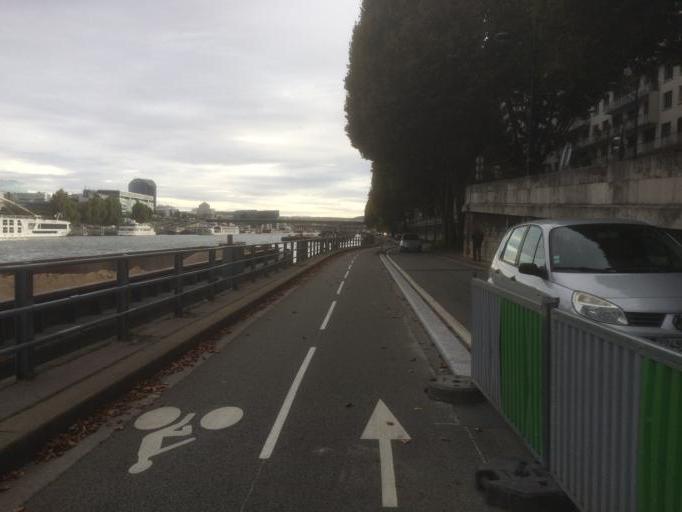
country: FR
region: Ile-de-France
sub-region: Departement des Hauts-de-Seine
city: Issy-les-Moulineaux
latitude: 48.8448
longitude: 2.2725
